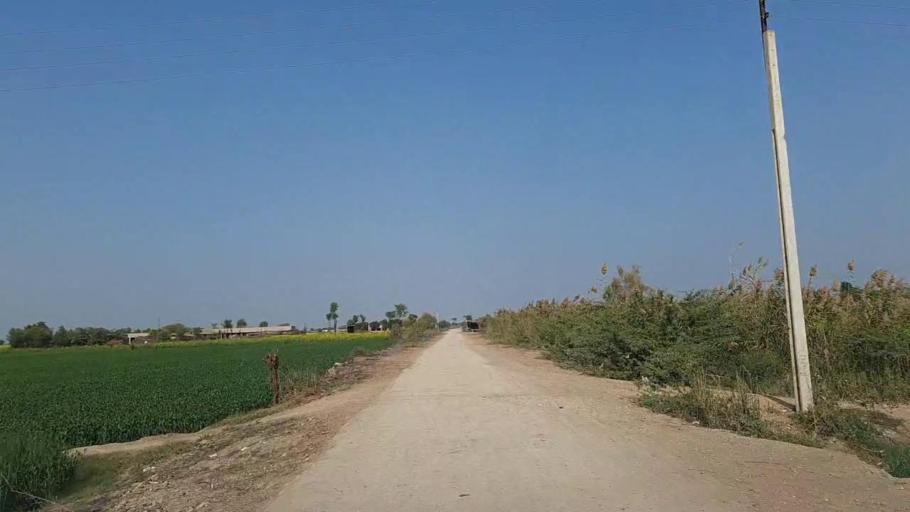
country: PK
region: Sindh
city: Nawabshah
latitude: 26.2801
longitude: 68.5136
